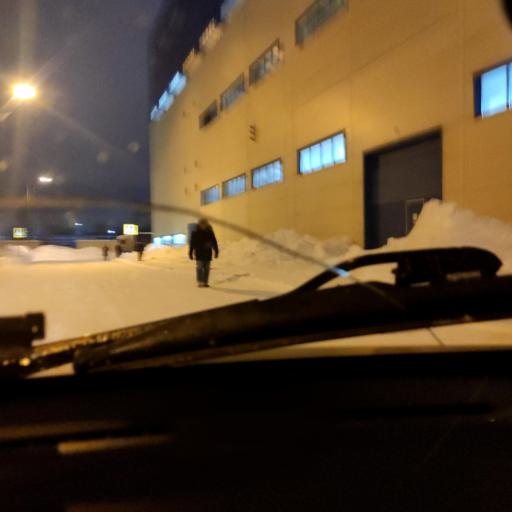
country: RU
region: Tatarstan
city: Staroye Arakchino
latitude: 55.8307
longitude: 49.0318
